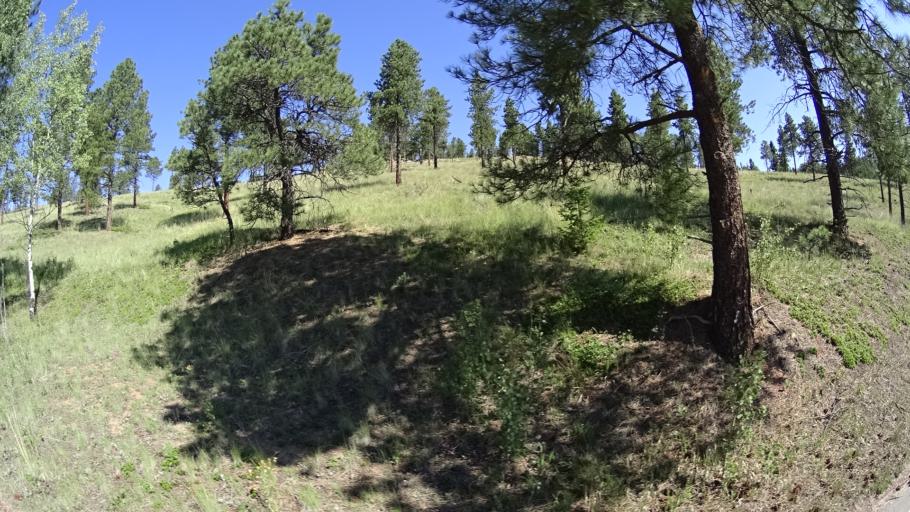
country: US
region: Colorado
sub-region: El Paso County
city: Cascade-Chipita Park
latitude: 38.9121
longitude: -105.0224
